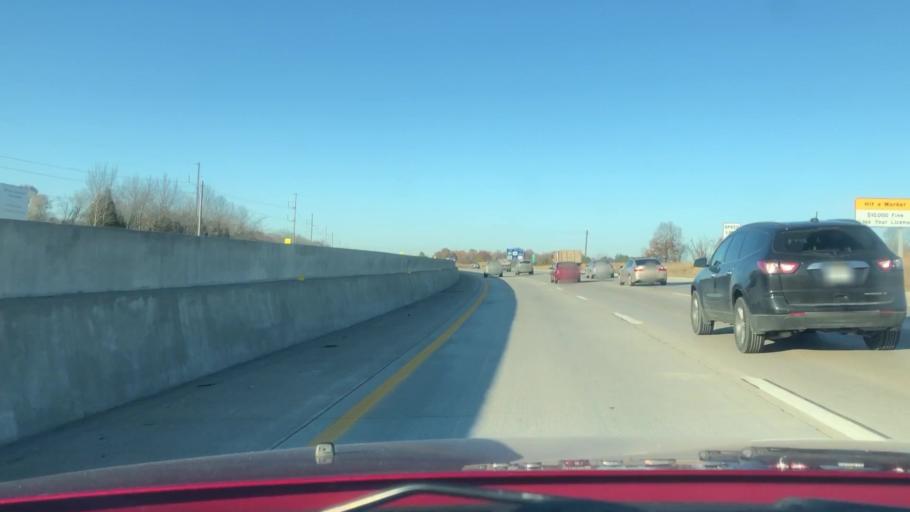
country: US
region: Missouri
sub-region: Greene County
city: Springfield
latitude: 37.1376
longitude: -93.2248
